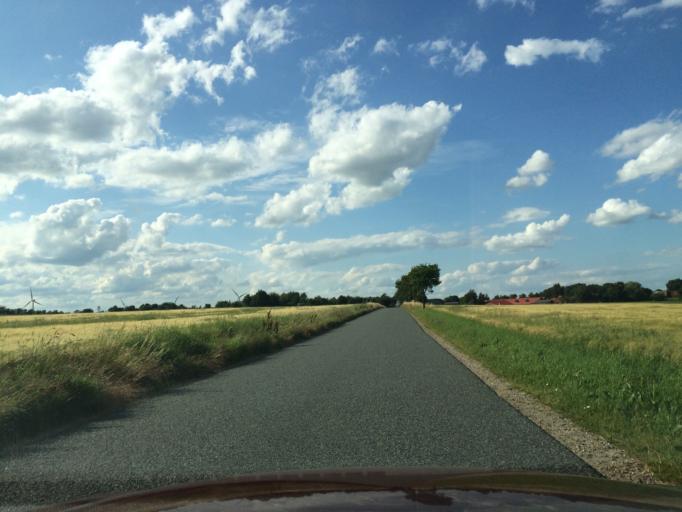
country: DK
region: Central Jutland
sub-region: Viborg Kommune
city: Bjerringbro
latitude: 56.2485
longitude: 9.7130
